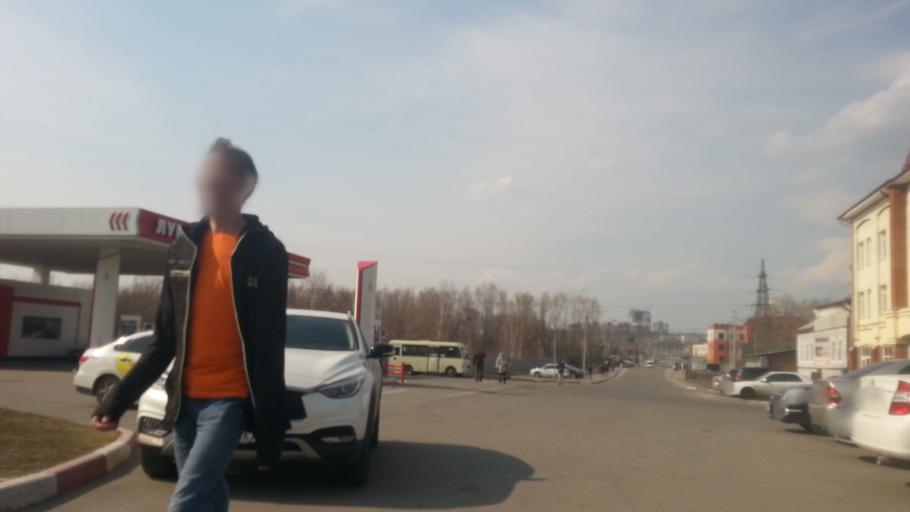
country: RU
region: Altai Krai
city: Zaton
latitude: 53.3264
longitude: 83.7932
